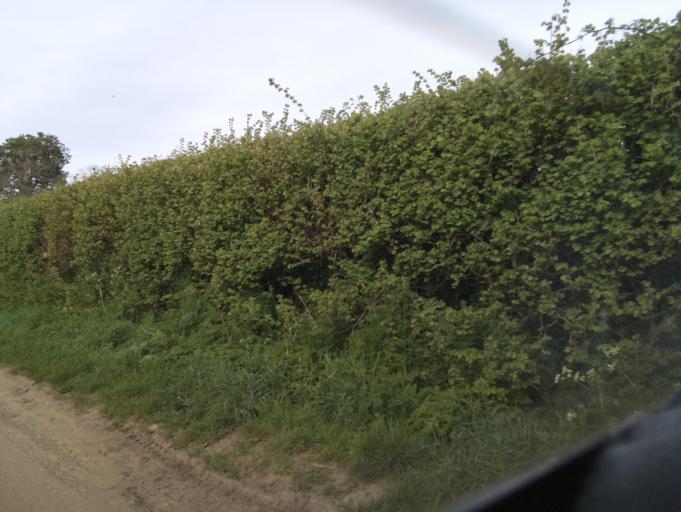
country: GB
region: England
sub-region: Somerset
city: Milborne Port
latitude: 50.9621
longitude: -2.4677
